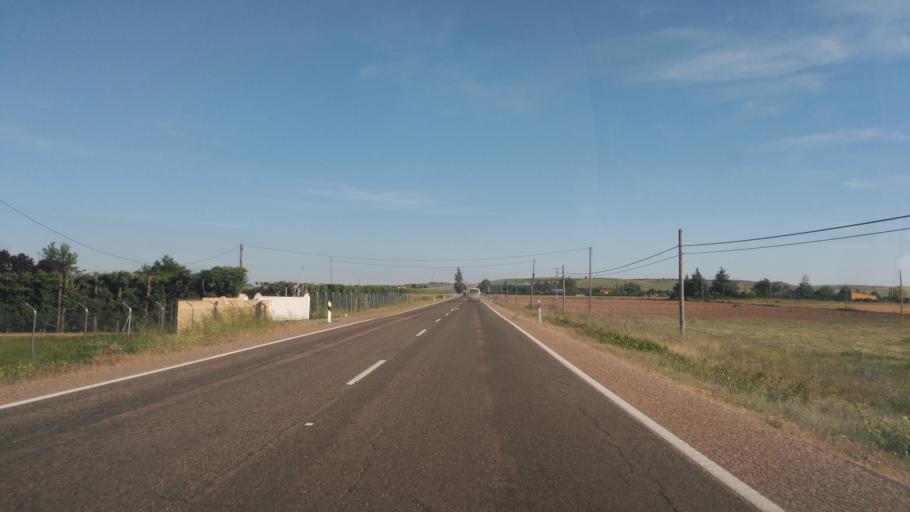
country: ES
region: Castille and Leon
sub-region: Provincia de Zamora
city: Morales del Vino
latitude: 41.4292
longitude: -5.7264
